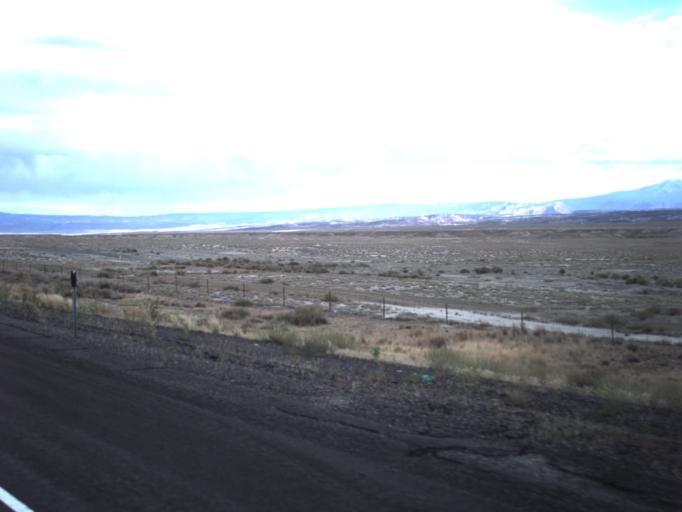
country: US
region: Utah
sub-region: Grand County
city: Moab
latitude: 38.9346
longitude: -109.4617
